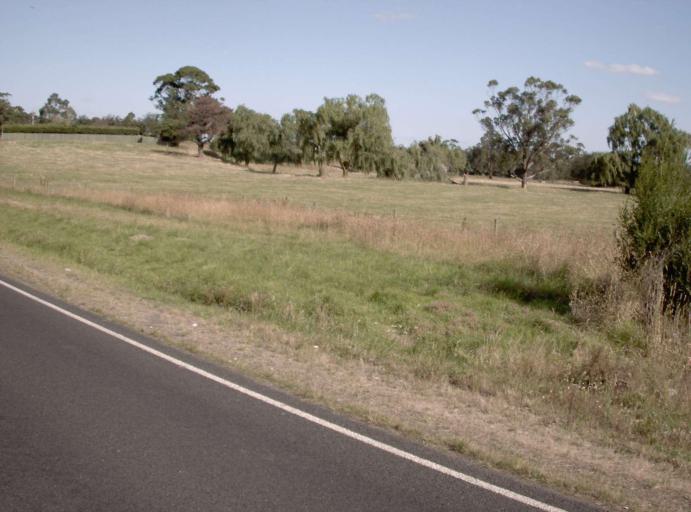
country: AU
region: Victoria
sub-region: Latrobe
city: Moe
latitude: -38.1630
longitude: 146.2704
